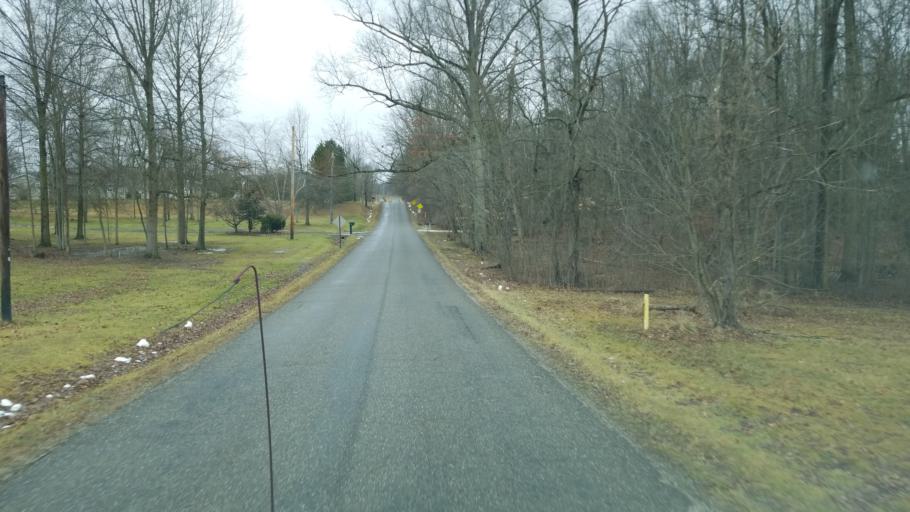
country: US
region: Ohio
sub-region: Portage County
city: Windham
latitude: 41.3394
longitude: -80.9764
